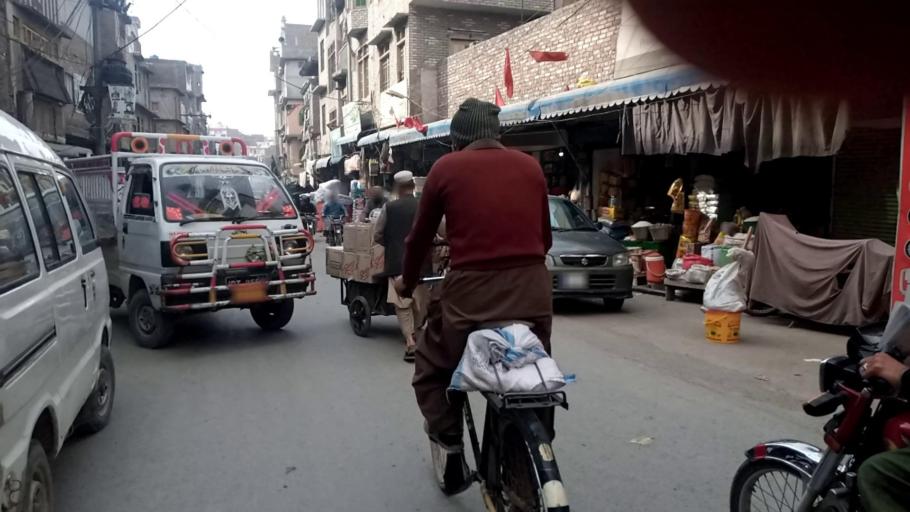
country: PK
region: Khyber Pakhtunkhwa
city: Peshawar
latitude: 34.0078
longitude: 71.5757
